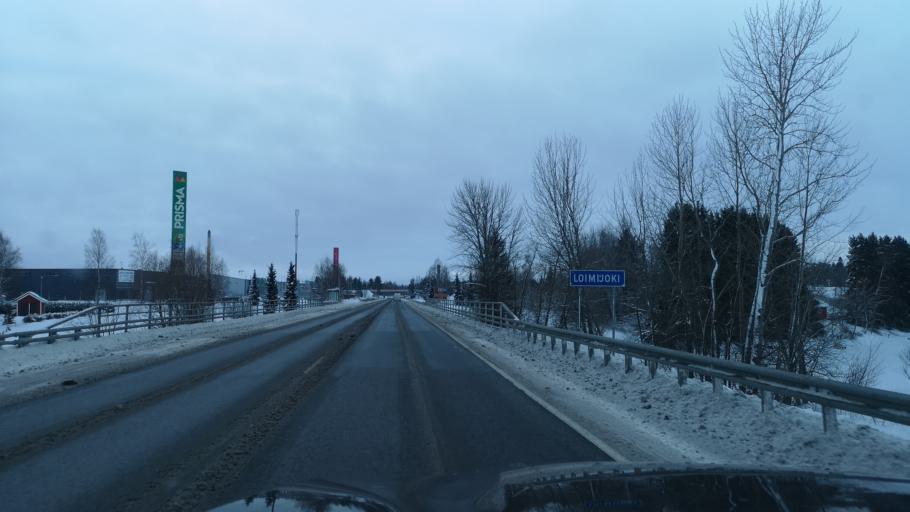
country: FI
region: Varsinais-Suomi
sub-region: Loimaa
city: Loimaa
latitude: 60.8590
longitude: 23.0449
